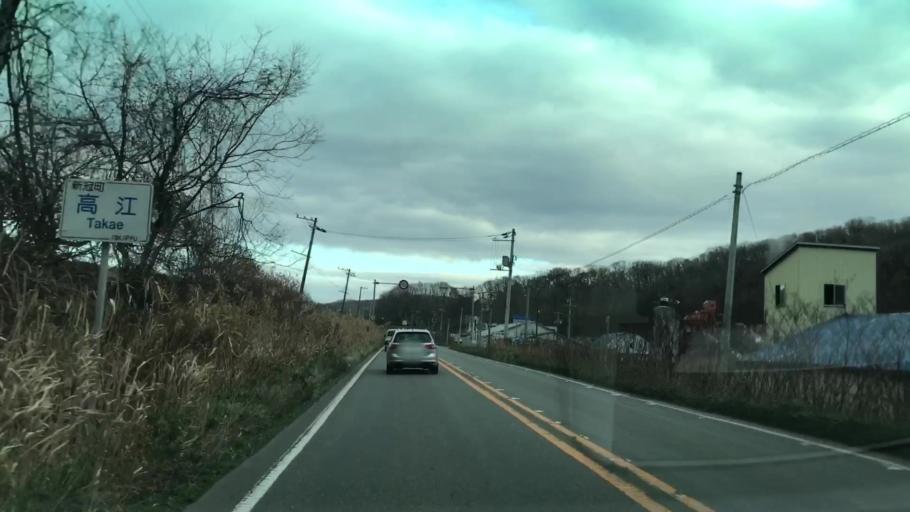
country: JP
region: Hokkaido
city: Shizunai-furukawacho
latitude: 42.3701
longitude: 142.2957
